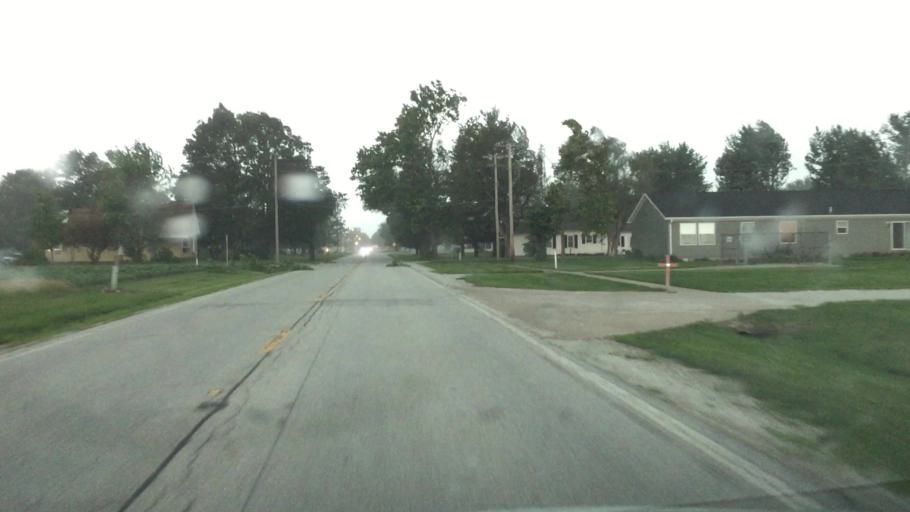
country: US
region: Illinois
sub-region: Adams County
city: Camp Point
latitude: 40.2315
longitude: -91.0570
